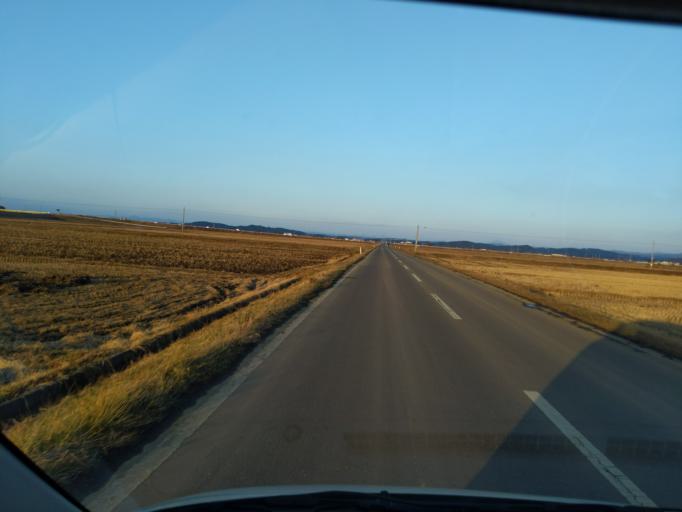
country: JP
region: Miyagi
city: Wakuya
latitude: 38.7127
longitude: 141.1555
